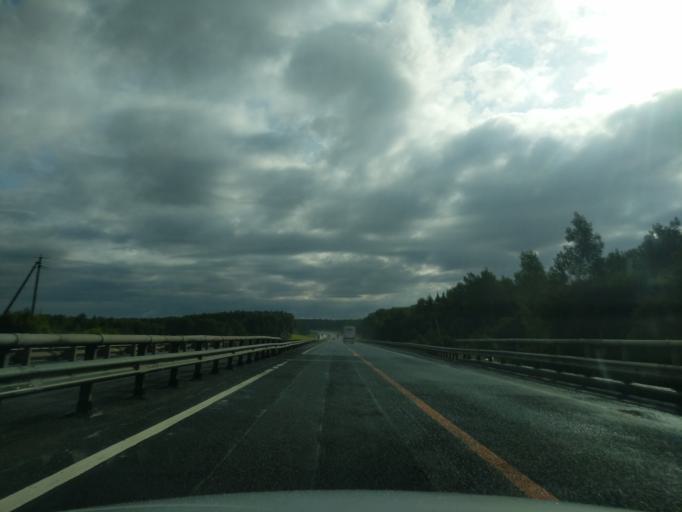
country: RU
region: Vladimir
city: Arsaki
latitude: 56.5117
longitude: 38.5313
